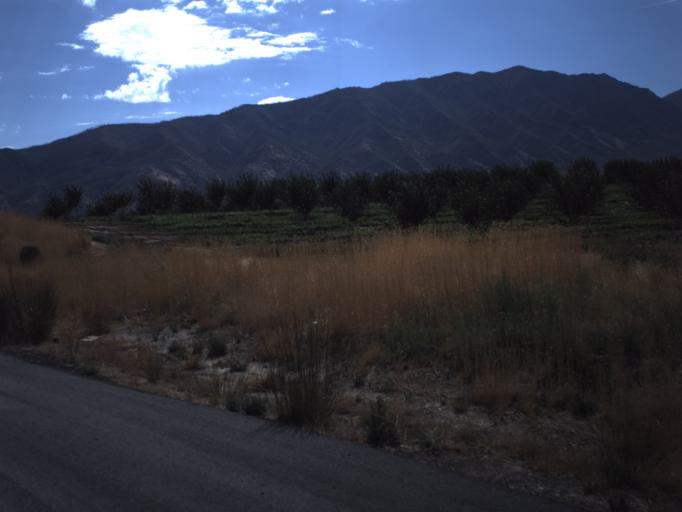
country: US
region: Utah
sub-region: Utah County
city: Genola
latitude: 39.9854
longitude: -111.8195
